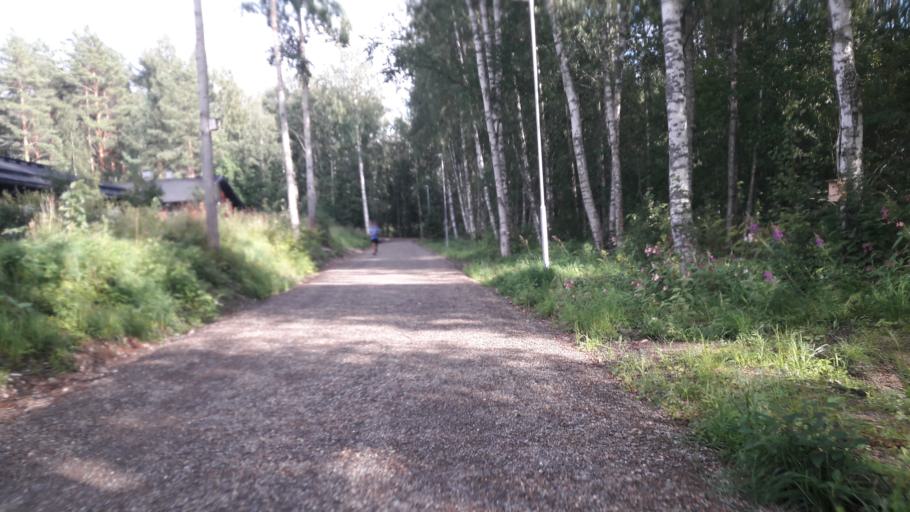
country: FI
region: North Karelia
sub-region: Joensuu
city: Joensuu
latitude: 62.5765
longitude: 29.7914
